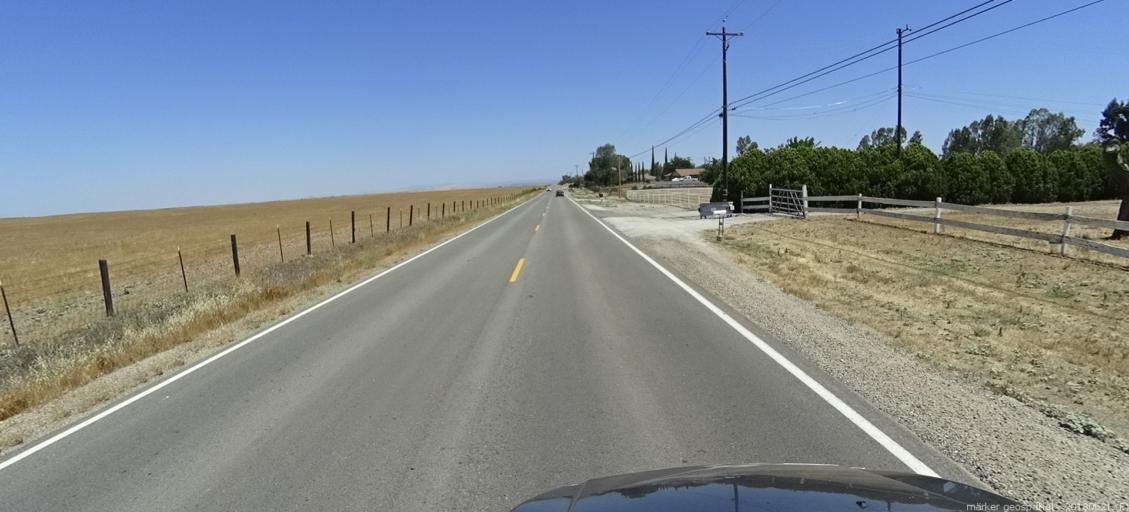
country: US
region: California
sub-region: Madera County
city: Bonadelle Ranchos-Madera Ranchos
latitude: 36.9721
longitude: -119.8938
